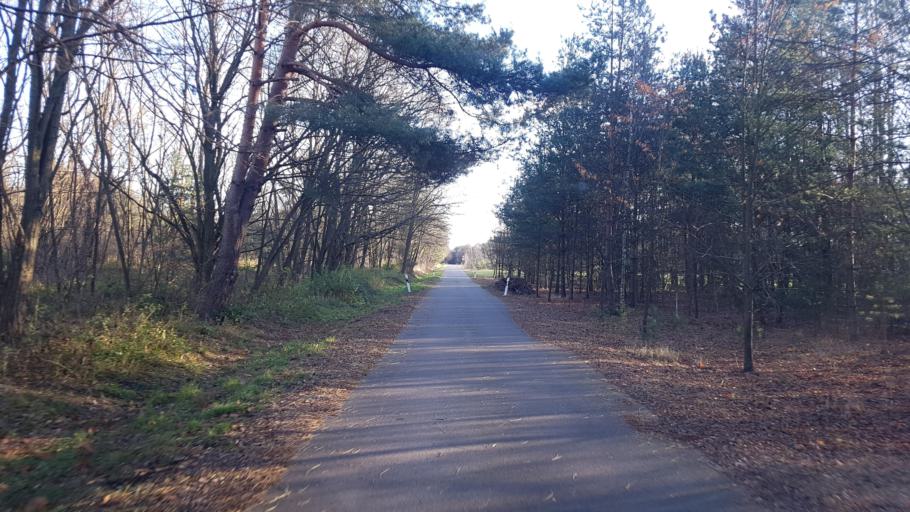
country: DE
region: Brandenburg
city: Heinersbruck
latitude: 51.7455
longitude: 14.5142
